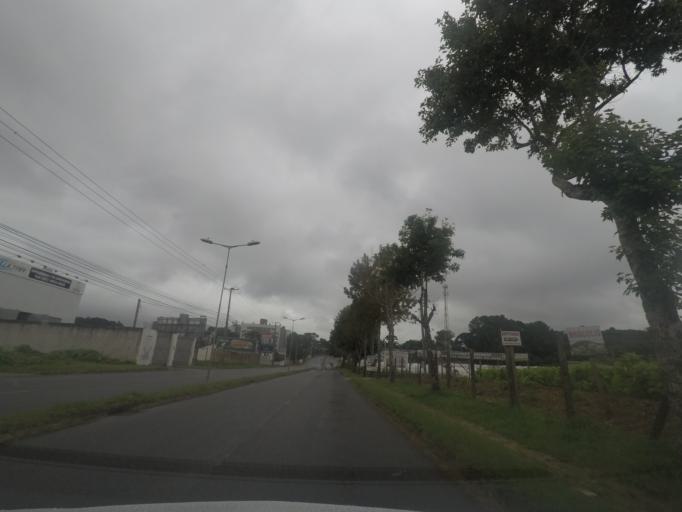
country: BR
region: Parana
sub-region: Pinhais
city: Pinhais
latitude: -25.3934
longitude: -49.1772
